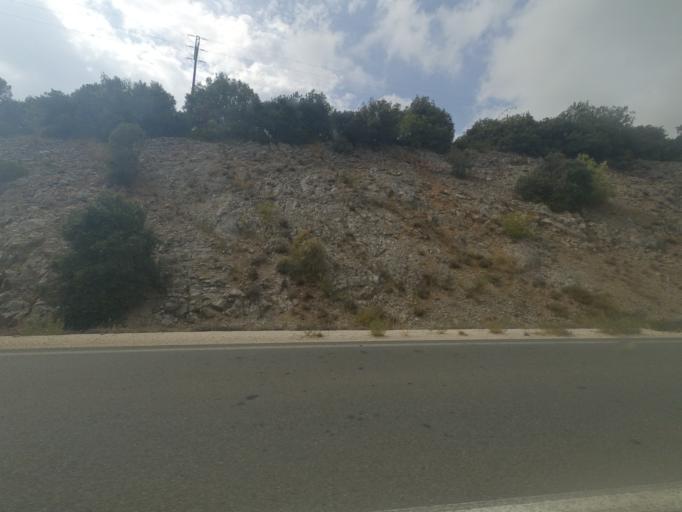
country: FR
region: Languedoc-Roussillon
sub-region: Departement de l'Herault
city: Les Matelles
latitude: 43.7267
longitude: 3.7948
